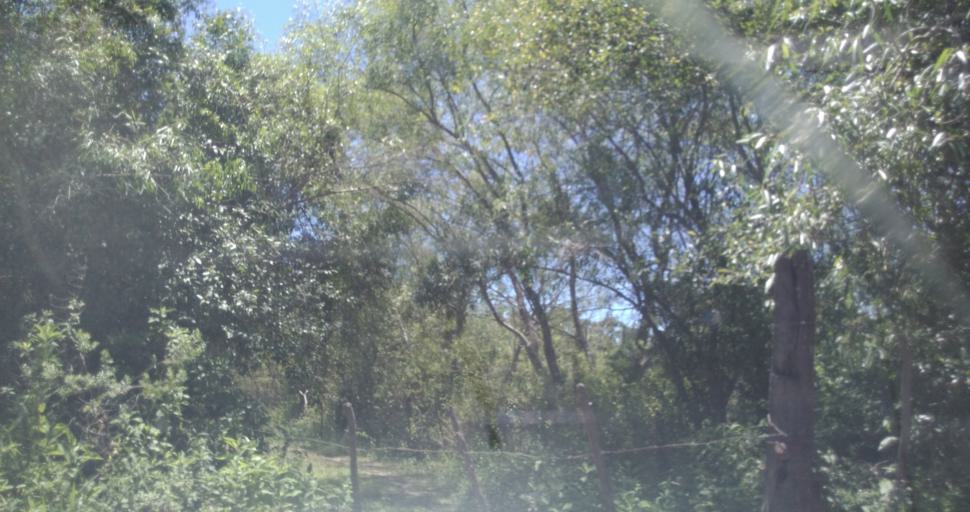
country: AR
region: Chaco
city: Fontana
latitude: -27.4141
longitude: -59.0087
